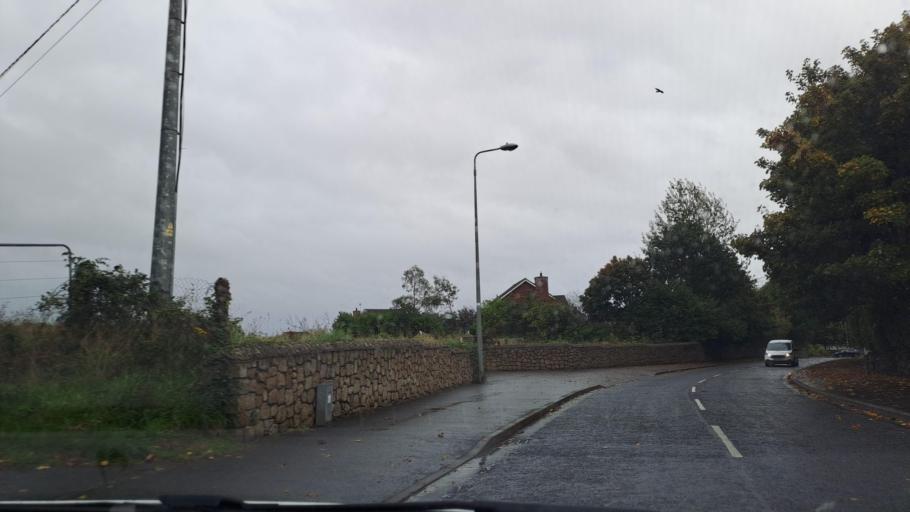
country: IE
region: Leinster
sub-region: Lu
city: Blackrock
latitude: 53.9620
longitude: -6.3771
